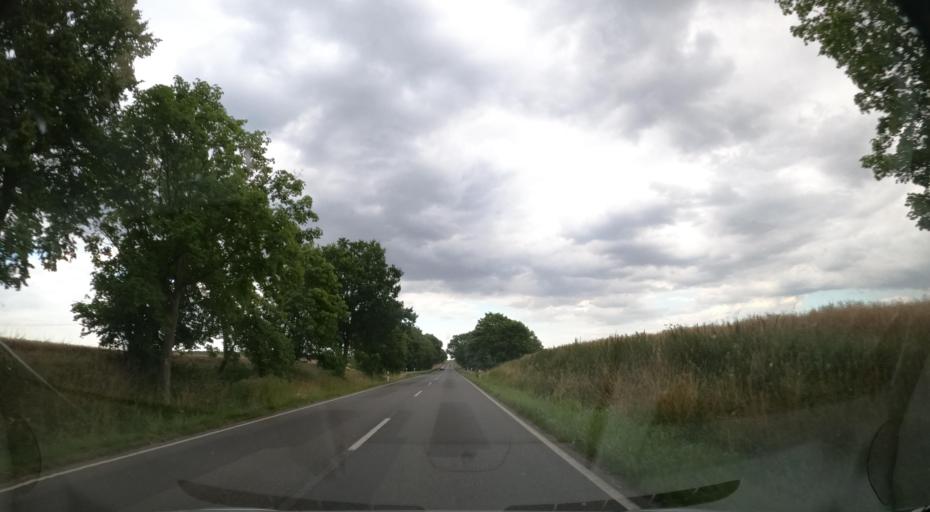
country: DE
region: Mecklenburg-Vorpommern
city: Woldegk
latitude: 53.4793
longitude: 13.6558
